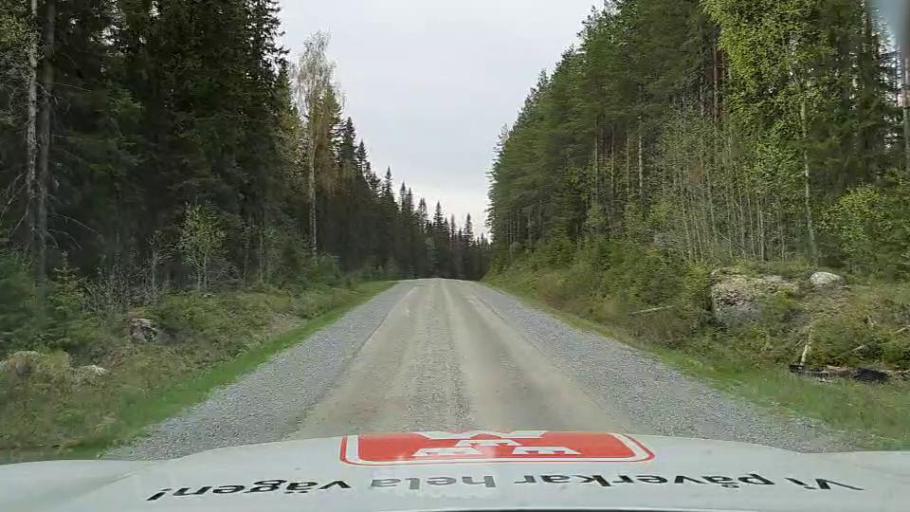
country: SE
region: Jaemtland
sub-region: OEstersunds Kommun
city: Brunflo
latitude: 62.6350
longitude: 14.9371
